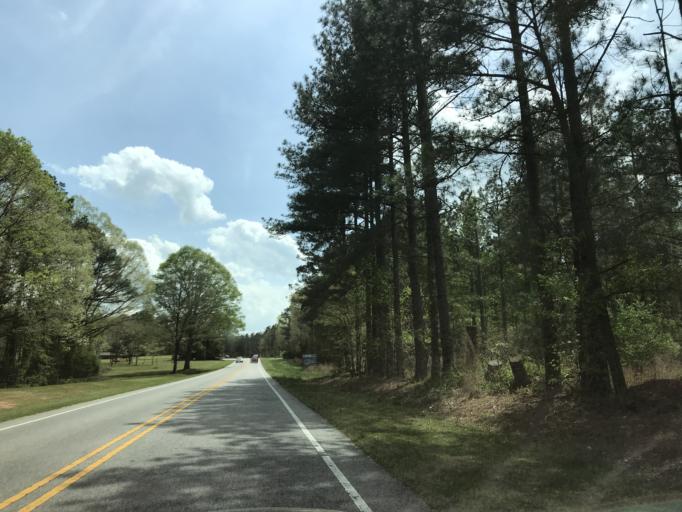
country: US
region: North Carolina
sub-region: Nash County
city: Spring Hope
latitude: 35.9662
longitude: -78.2089
